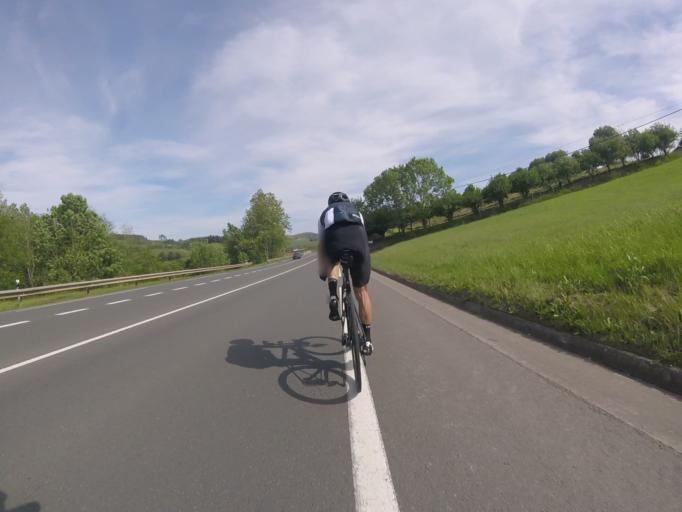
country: ES
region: Basque Country
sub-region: Provincia de Guipuzcoa
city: Cestona
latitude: 43.2608
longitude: -2.2715
